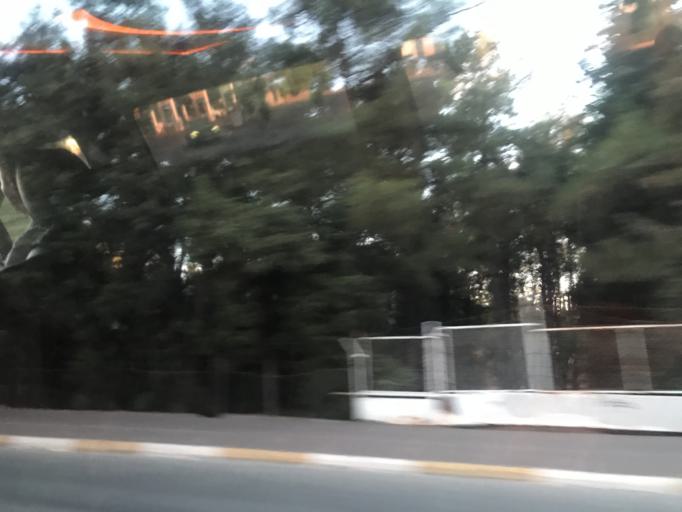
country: TR
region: Antalya
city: Antalya
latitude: 36.9164
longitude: 30.6743
